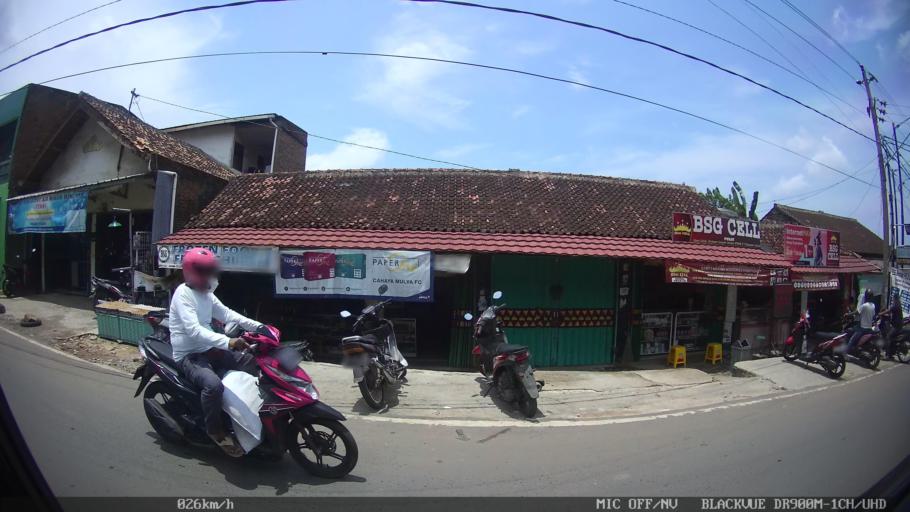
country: ID
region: Lampung
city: Kedaton
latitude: -5.3930
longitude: 105.2488
